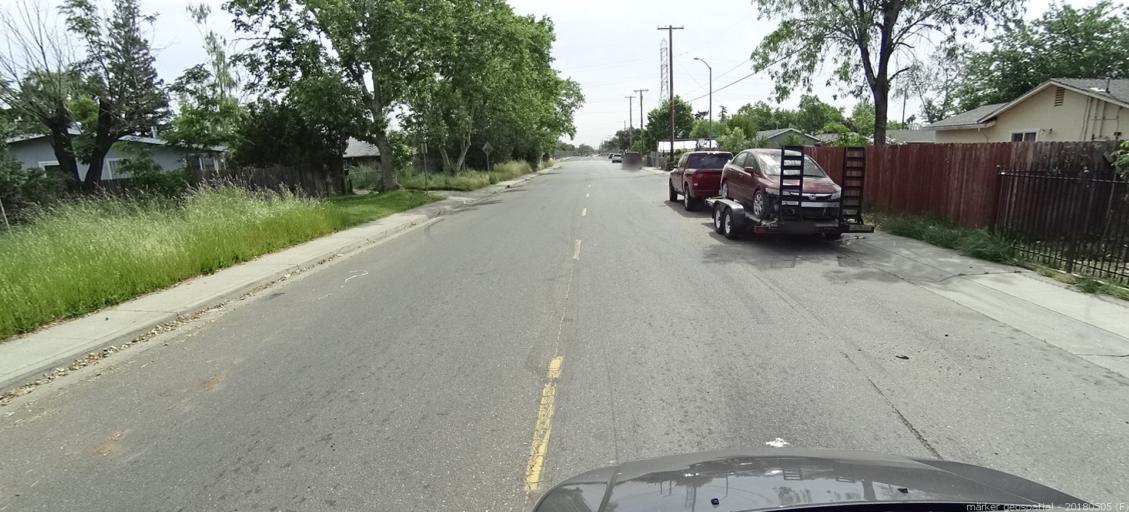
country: US
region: California
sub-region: Sacramento County
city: Rio Linda
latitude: 38.6400
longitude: -121.4249
